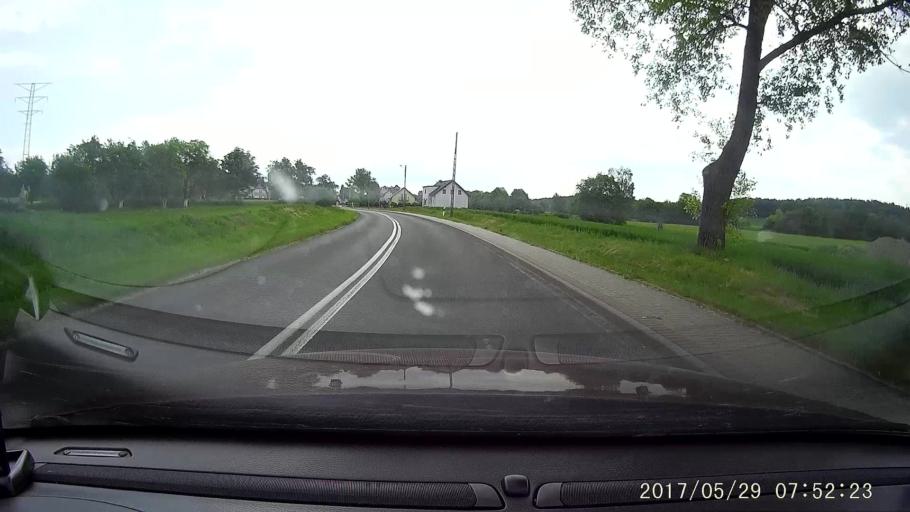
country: PL
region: Lower Silesian Voivodeship
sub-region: Powiat zlotoryjski
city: Olszanica
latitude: 51.2166
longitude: 15.7175
